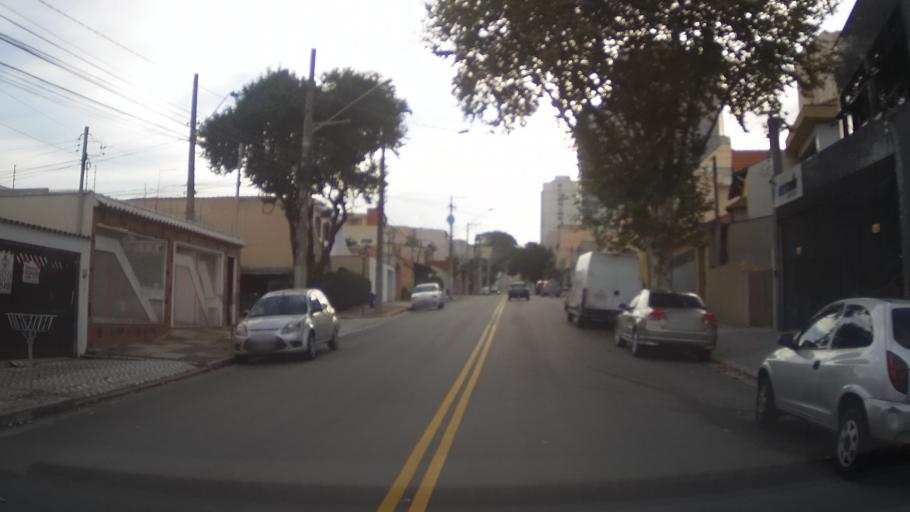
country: BR
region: Sao Paulo
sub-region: Sao Caetano Do Sul
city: Sao Caetano do Sul
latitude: -23.6245
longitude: -46.5580
